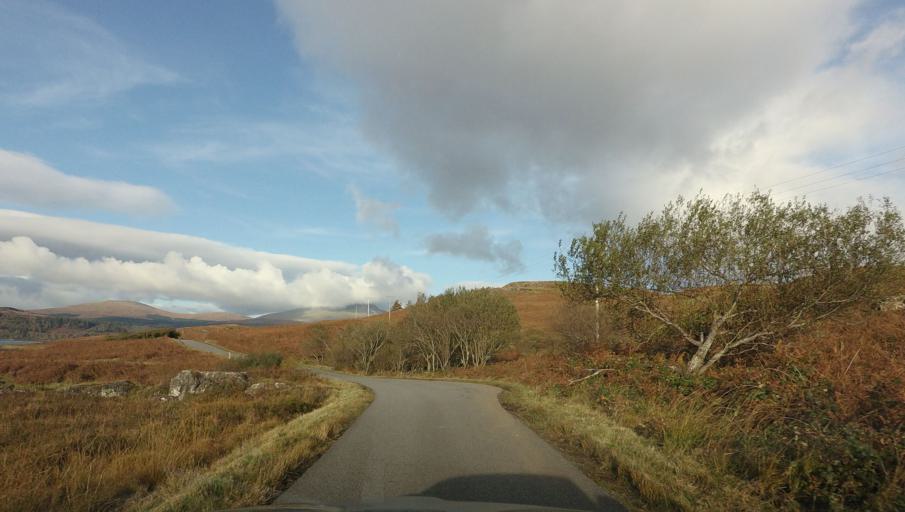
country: GB
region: Scotland
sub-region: Argyll and Bute
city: Isle Of Mull
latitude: 56.3468
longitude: -6.0888
